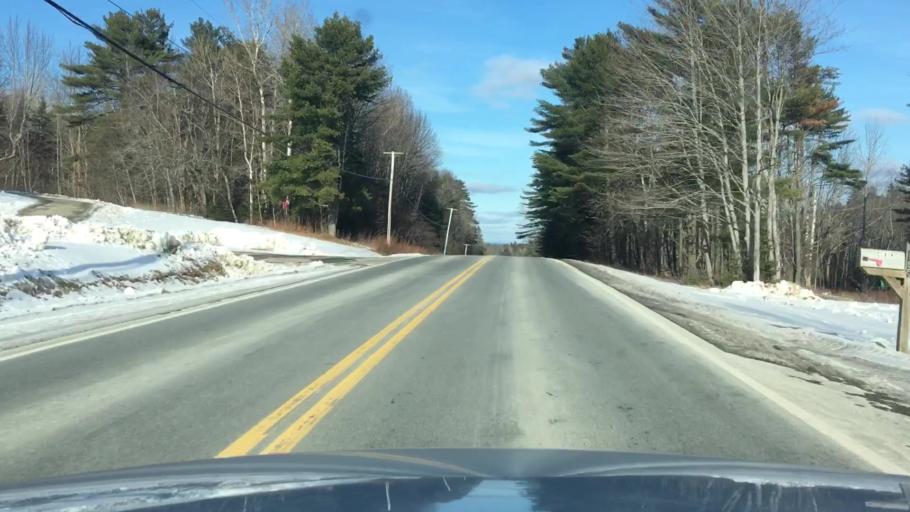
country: US
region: Maine
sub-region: Penobscot County
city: Holden
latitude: 44.7452
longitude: -68.6155
